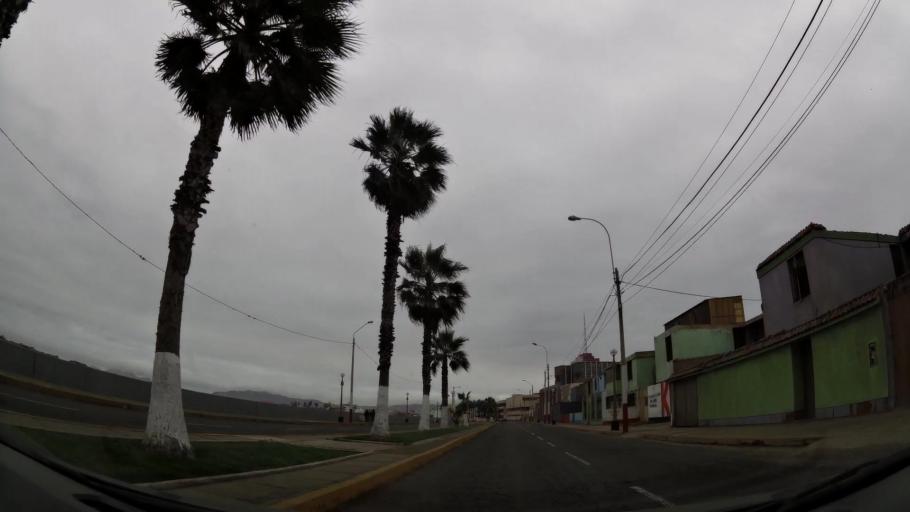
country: PE
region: Callao
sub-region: Callao
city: Callao
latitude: -12.0664
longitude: -77.1540
